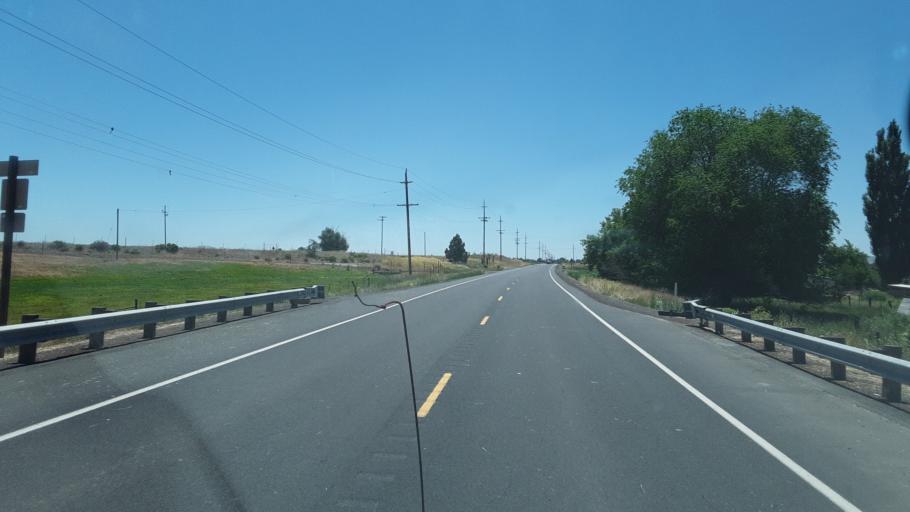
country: US
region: California
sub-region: Siskiyou County
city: Tulelake
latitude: 42.0401
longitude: -121.6236
